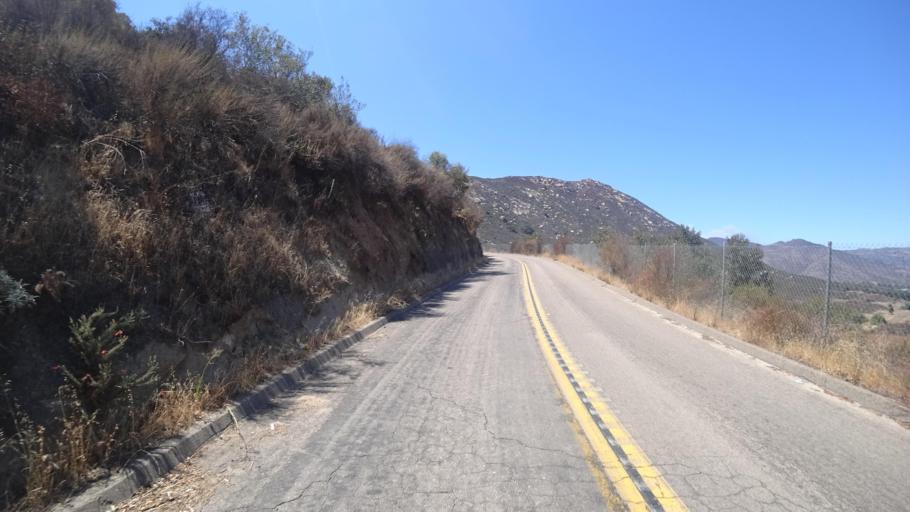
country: US
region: California
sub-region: San Diego County
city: Rainbow
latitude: 33.3461
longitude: -117.0811
